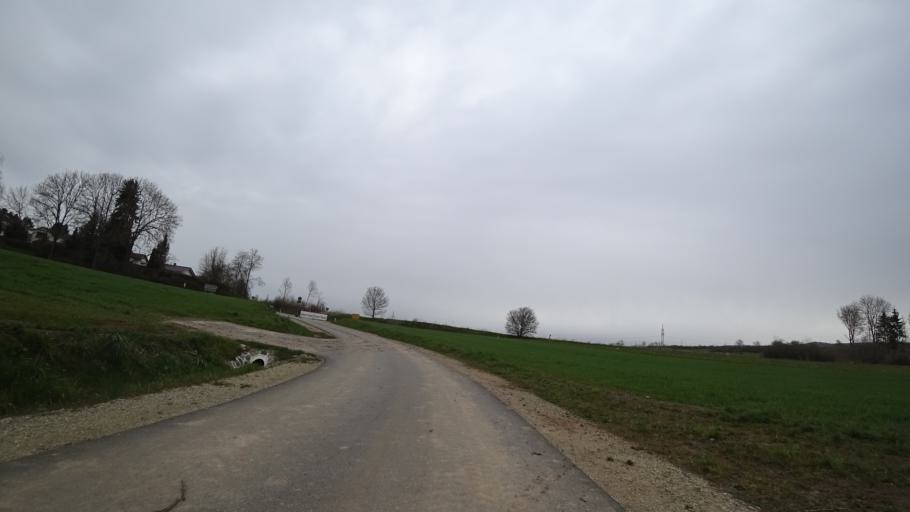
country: DE
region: Hesse
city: Grebenstein
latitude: 51.4271
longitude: 9.4376
